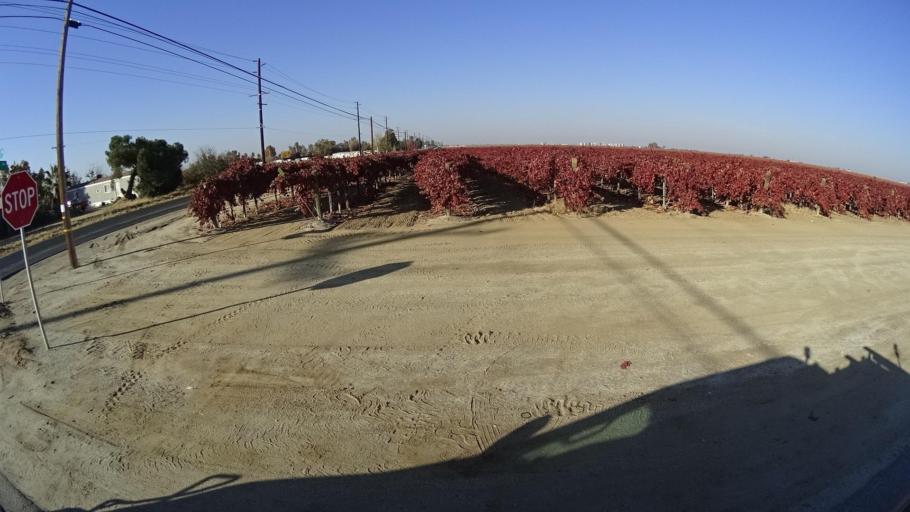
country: US
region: California
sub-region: Tulare County
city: Richgrove
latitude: 35.7762
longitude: -119.1697
